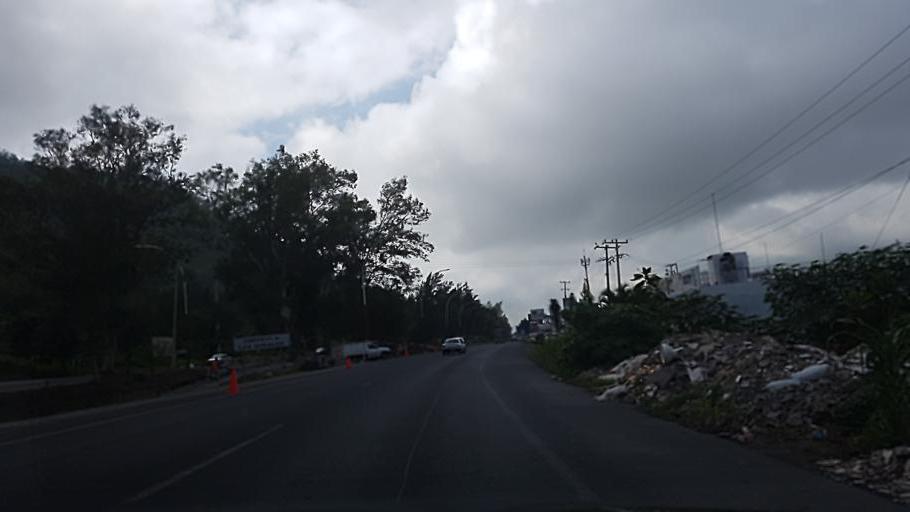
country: MX
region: Nayarit
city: Tepic
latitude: 21.5032
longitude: -104.9197
